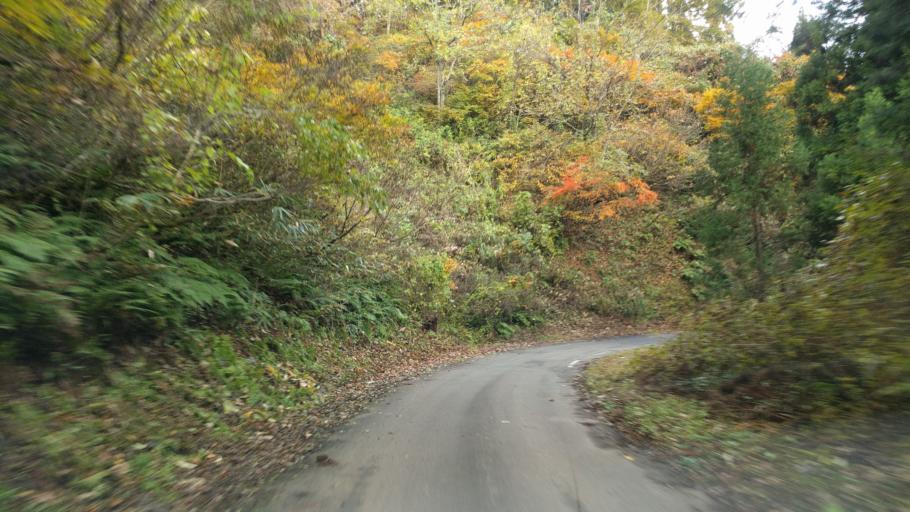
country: JP
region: Fukushima
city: Kitakata
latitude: 37.3981
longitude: 139.7112
